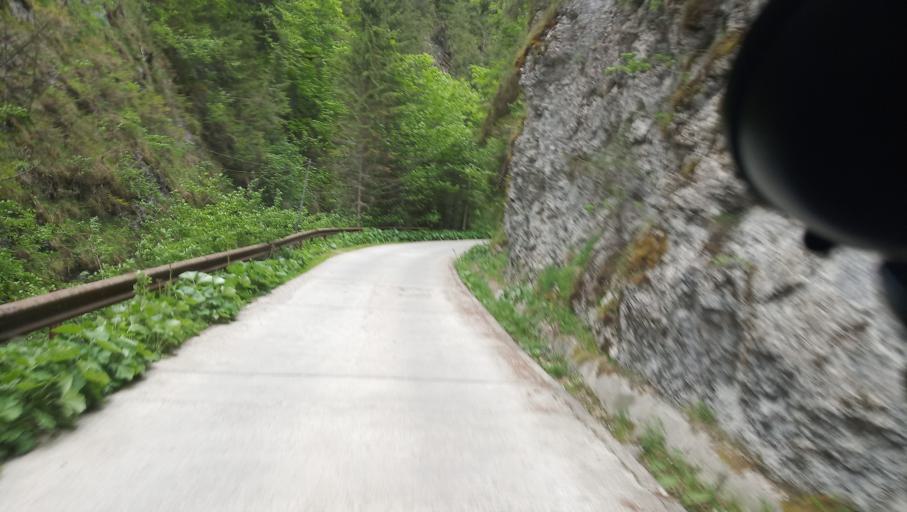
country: RO
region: Alba
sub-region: Comuna Scarisoara
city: Scarisoara
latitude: 46.4635
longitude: 22.8357
